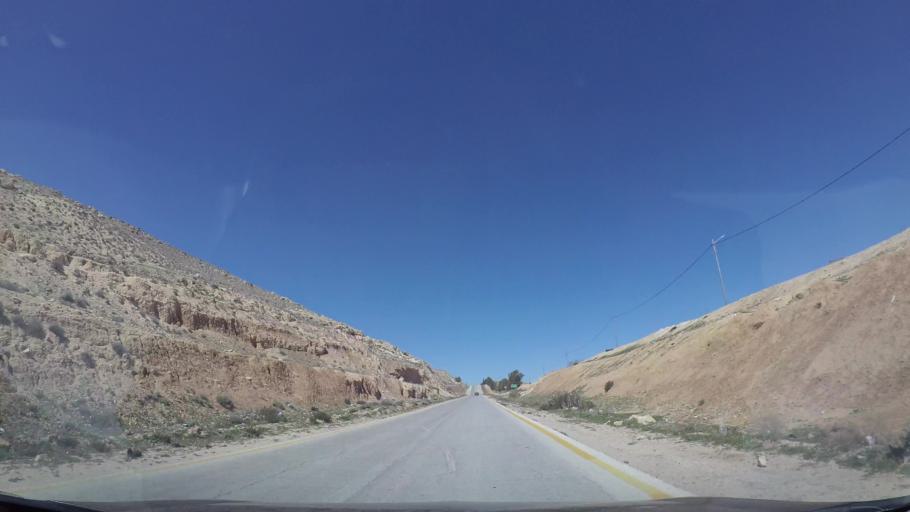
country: JO
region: Tafielah
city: At Tafilah
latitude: 30.8437
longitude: 35.5611
